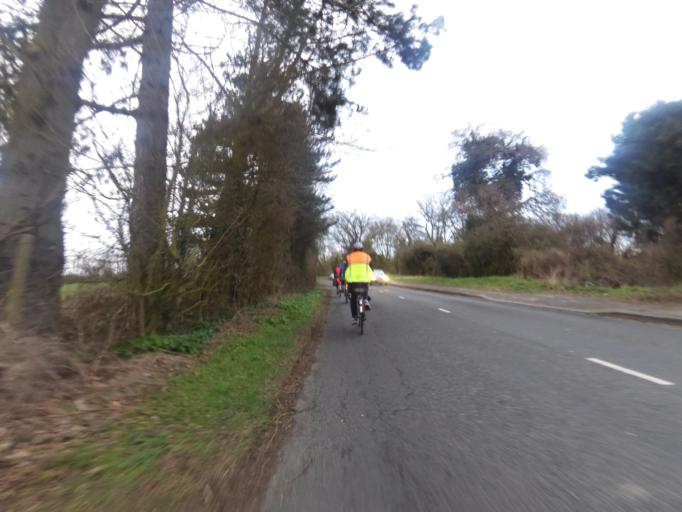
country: GB
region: England
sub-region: Suffolk
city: Ipswich
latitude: 52.0744
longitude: 1.1637
